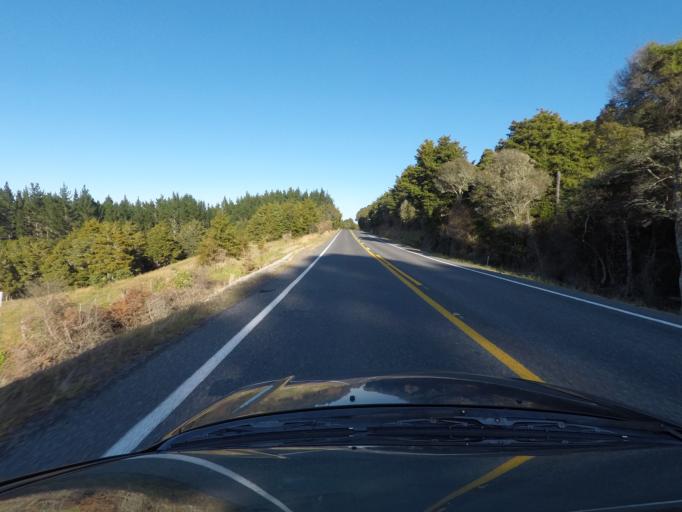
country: NZ
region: Northland
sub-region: Far North District
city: Kawakawa
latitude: -35.4797
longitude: 174.1170
